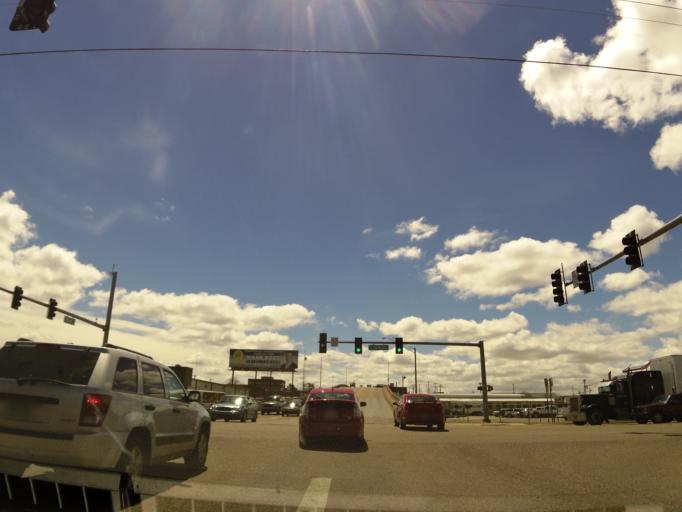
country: US
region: Arkansas
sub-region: Craighead County
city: Jonesboro
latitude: 35.8455
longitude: -90.7047
